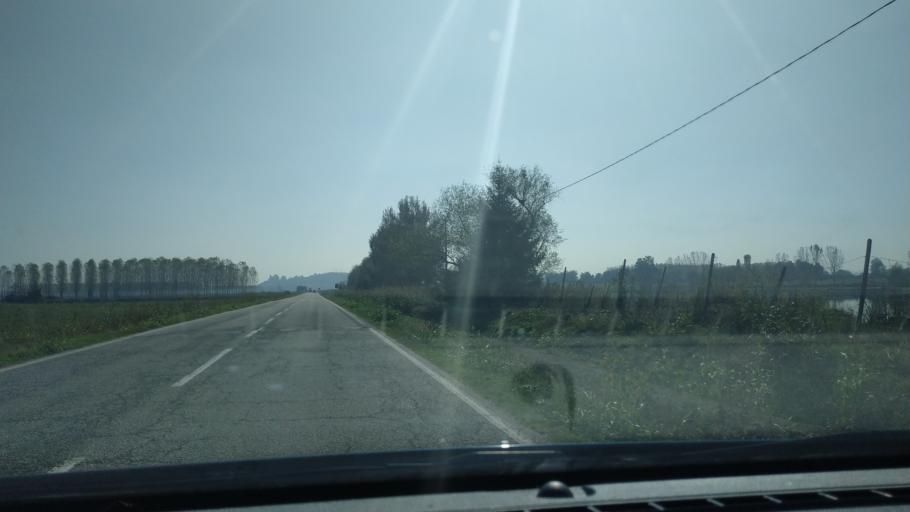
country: IT
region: Piedmont
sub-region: Provincia di Alessandria
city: Giarole
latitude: 45.0788
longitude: 8.5666
